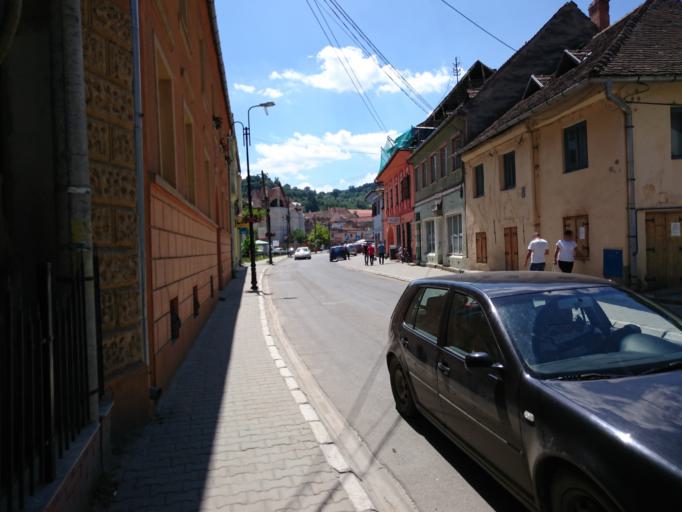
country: RO
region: Mures
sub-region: Municipiul Sighisoara
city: Sighisoara
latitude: 46.2206
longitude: 24.7946
